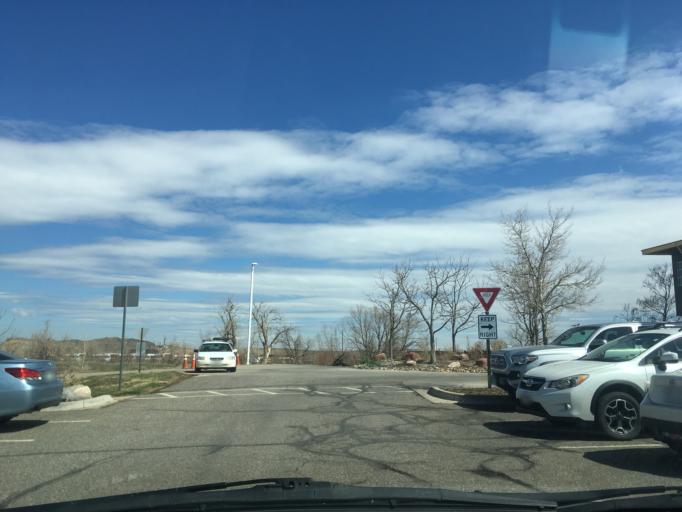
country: US
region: Colorado
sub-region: Boulder County
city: Gunbarrel
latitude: 40.0177
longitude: -105.2101
